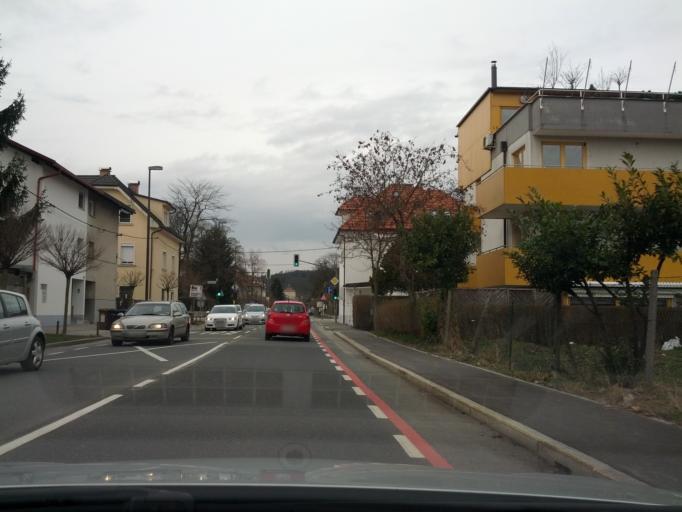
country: SI
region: Ljubljana
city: Ljubljana
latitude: 46.0413
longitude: 14.4994
